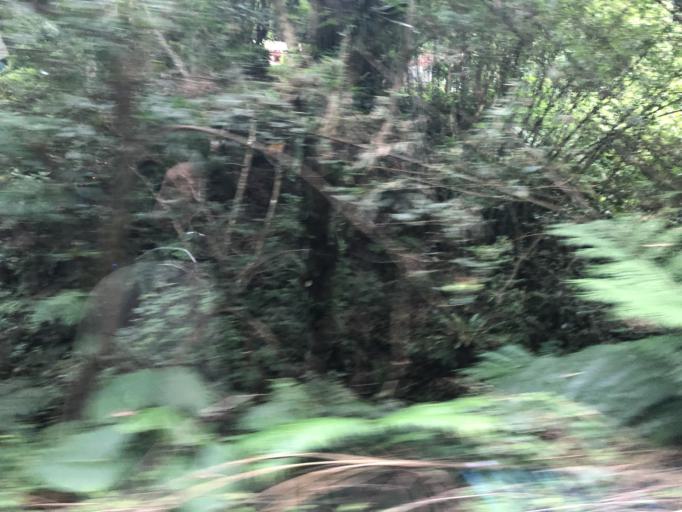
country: TW
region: Taiwan
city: Daxi
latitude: 24.9076
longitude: 121.3344
